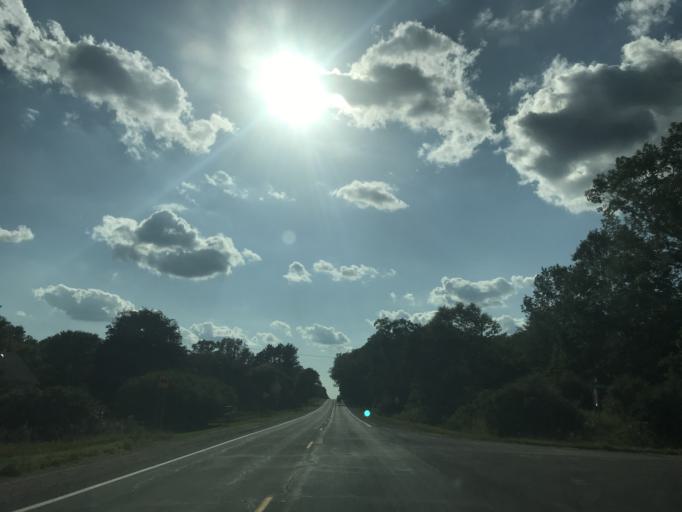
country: US
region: Michigan
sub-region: Newaygo County
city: White Cloud
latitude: 43.5684
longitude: -85.7912
